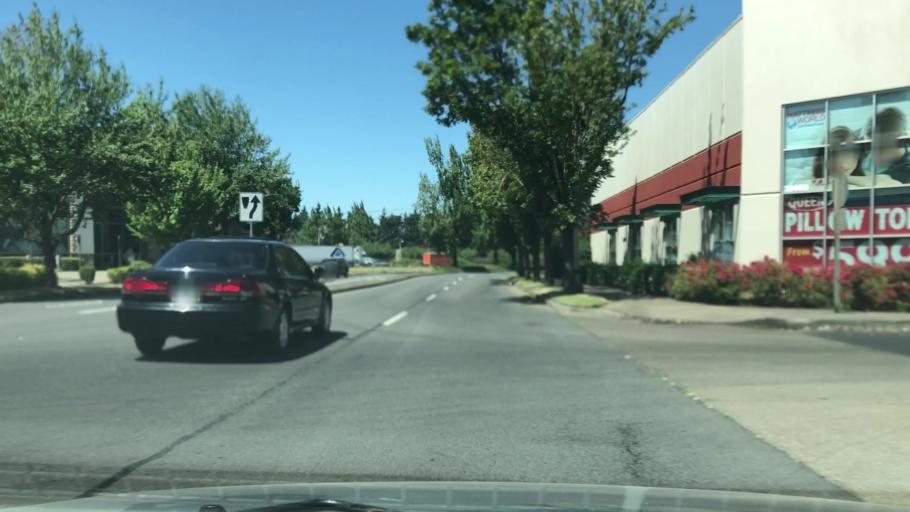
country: US
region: Oregon
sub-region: Clackamas County
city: Wilsonville
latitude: 45.3052
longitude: -122.7671
